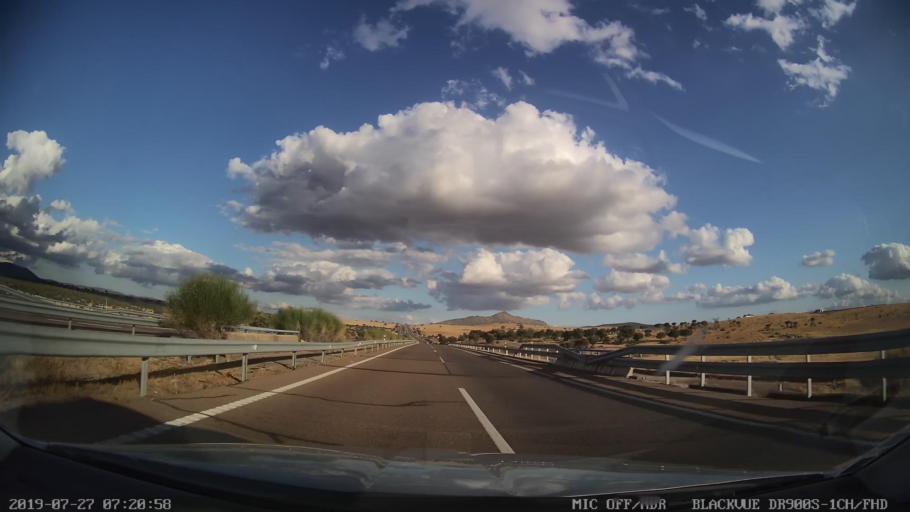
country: ES
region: Extremadura
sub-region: Provincia de Caceres
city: Santa Cruz de la Sierra
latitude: 39.3704
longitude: -5.8776
